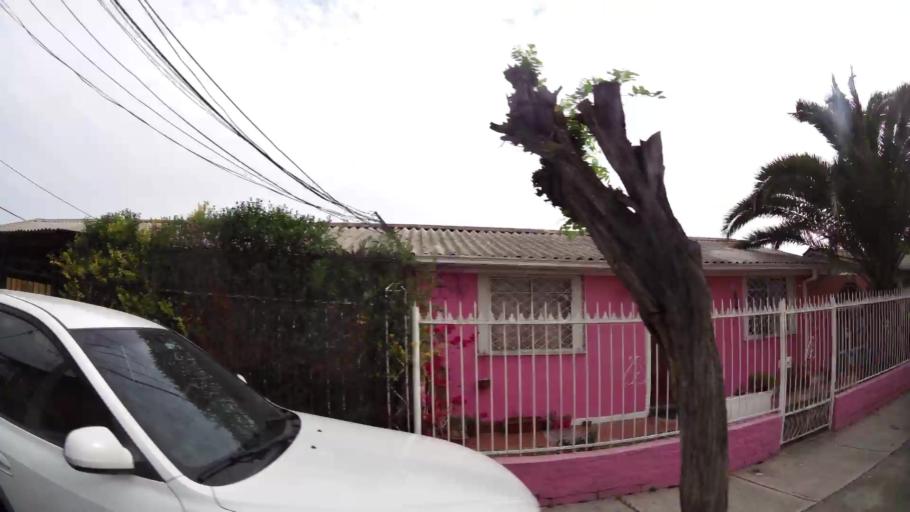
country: CL
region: Santiago Metropolitan
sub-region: Provincia de Santiago
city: Lo Prado
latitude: -33.5152
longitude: -70.7541
